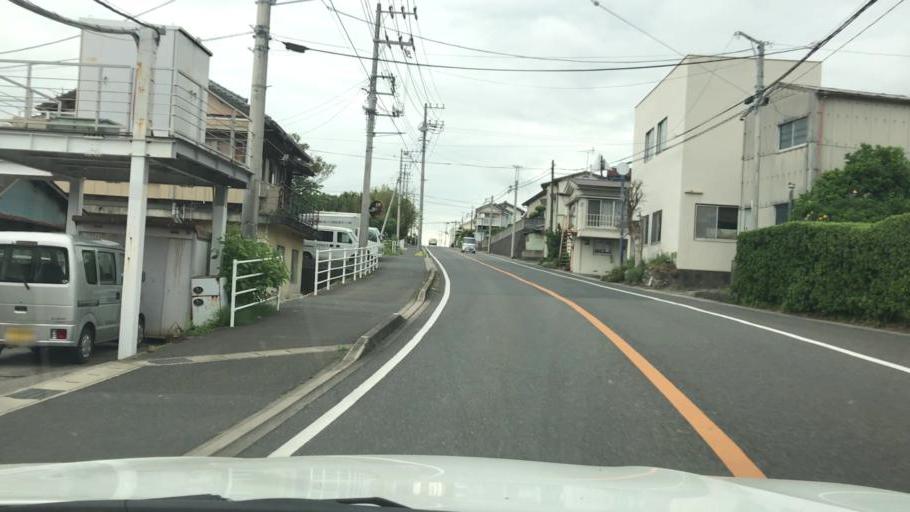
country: JP
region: Chiba
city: Kawaguchi
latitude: 35.1232
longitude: 140.0946
